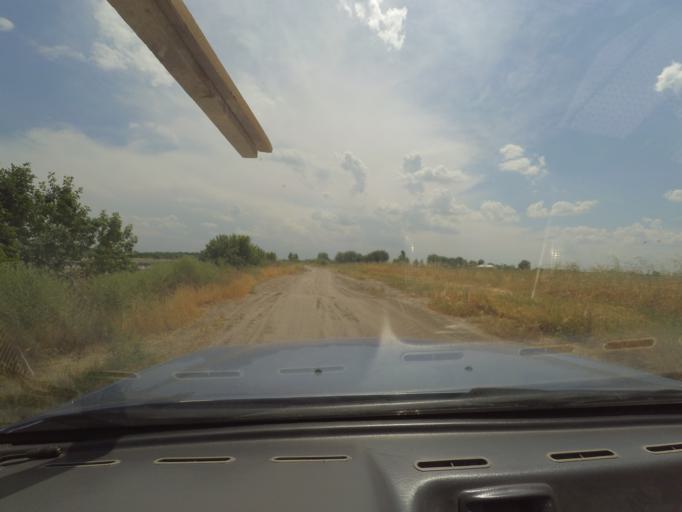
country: TJ
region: Viloyati Sughd
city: Buston
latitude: 40.5426
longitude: 69.0790
